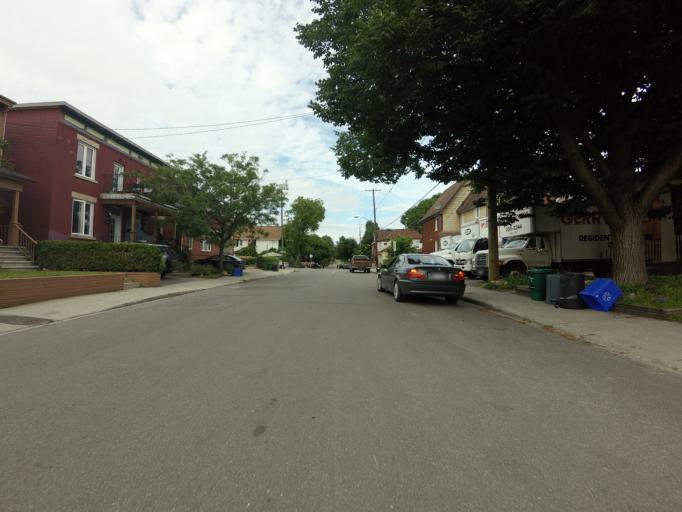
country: CA
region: Ontario
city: Ottawa
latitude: 45.4077
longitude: -75.6984
